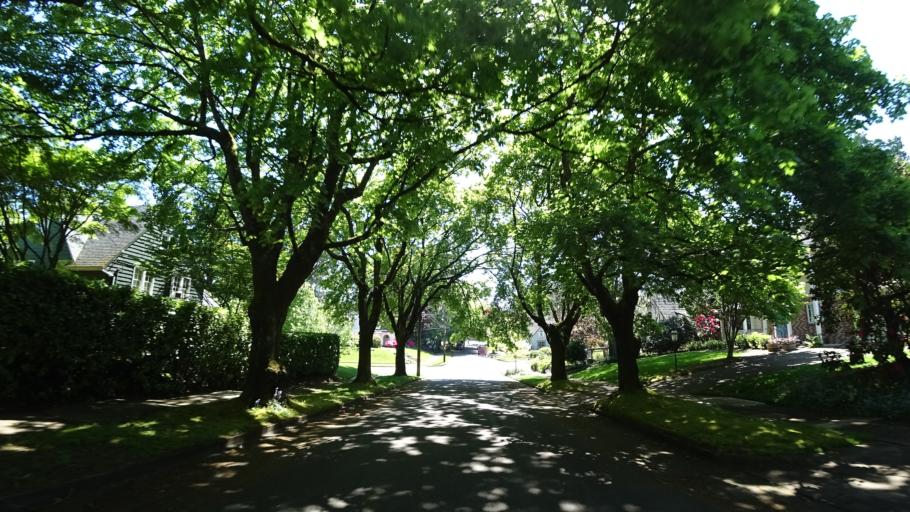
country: US
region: Oregon
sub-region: Clackamas County
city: Milwaukie
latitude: 45.4745
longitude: -122.6324
